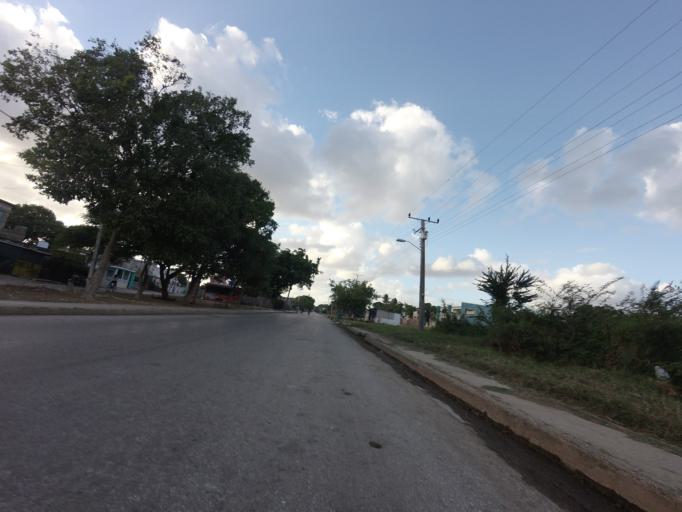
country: CU
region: Ciego de Avila
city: Ciego de Avila
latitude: 21.8294
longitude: -78.7525
